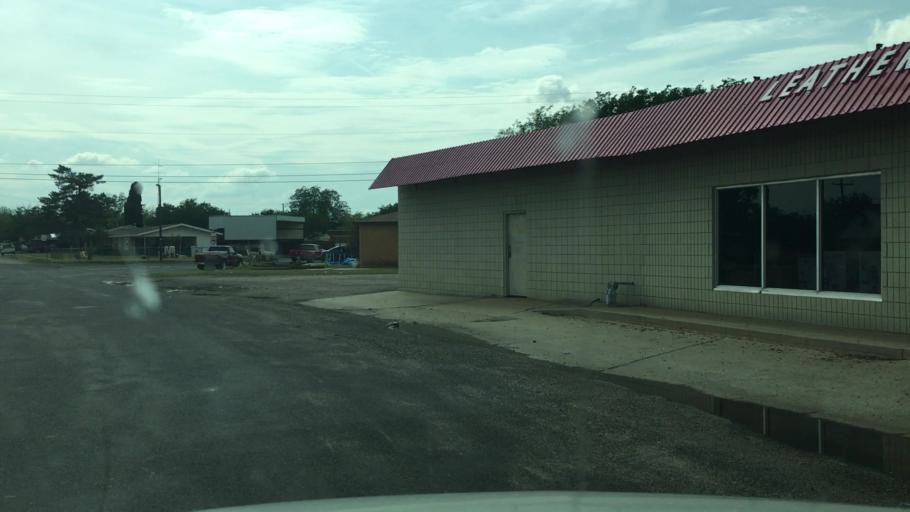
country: US
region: Texas
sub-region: Dawson County
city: Lamesa
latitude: 32.7515
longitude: -101.9510
